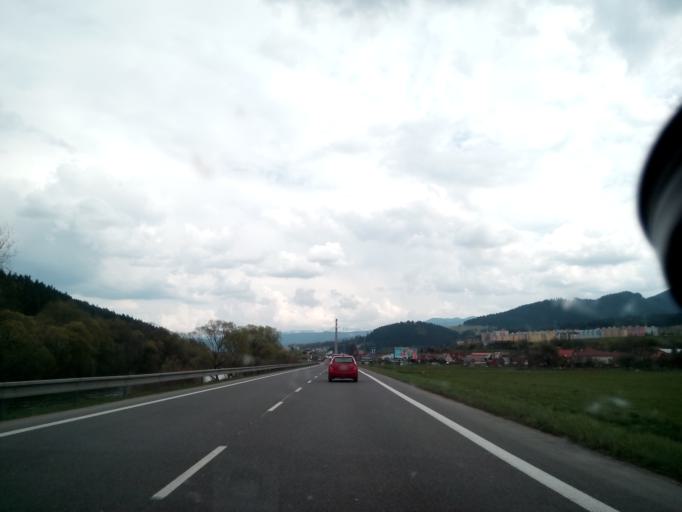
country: SK
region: Zilinsky
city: Ruzomberok
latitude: 49.0954
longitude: 19.2605
